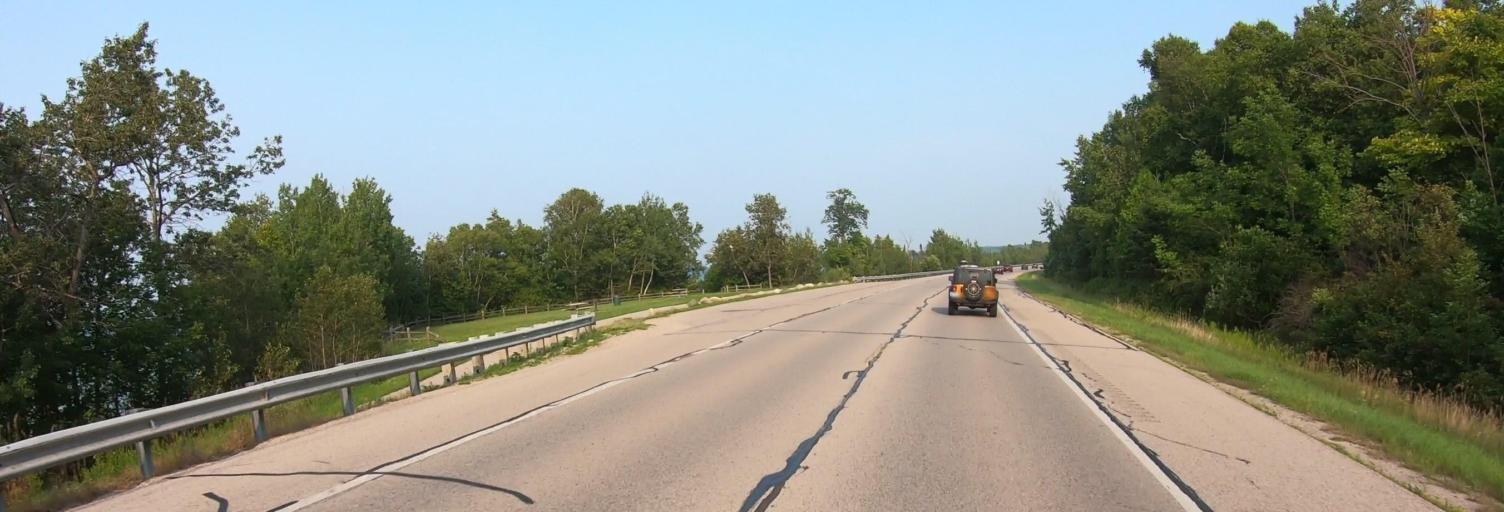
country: US
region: Michigan
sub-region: Charlevoix County
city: Charlevoix
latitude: 45.3682
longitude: -85.1310
